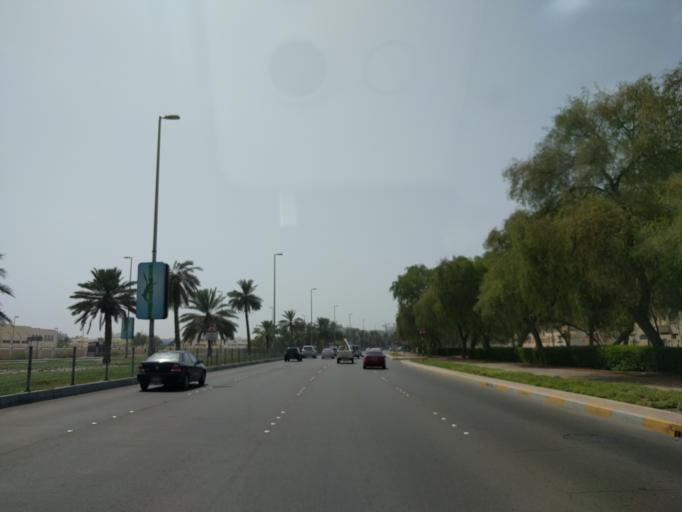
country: AE
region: Abu Dhabi
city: Abu Dhabi
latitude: 24.4423
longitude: 54.4059
